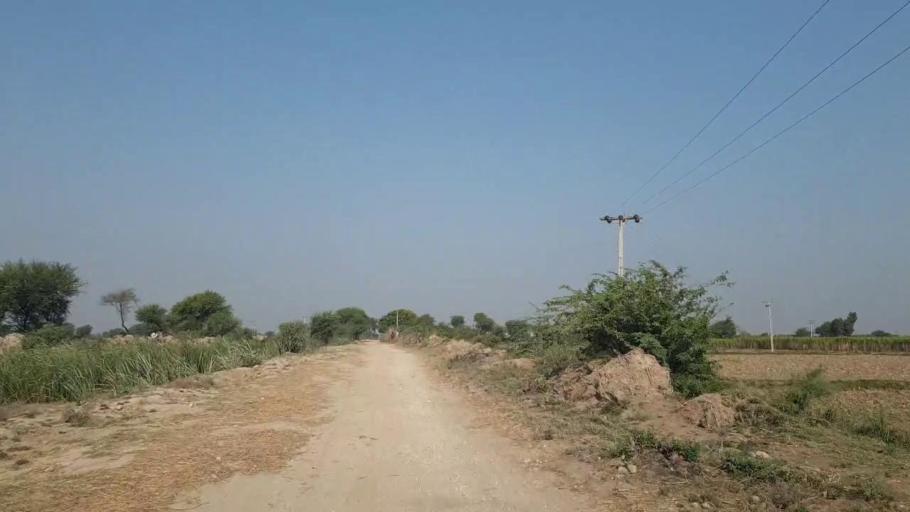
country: PK
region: Sindh
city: Matli
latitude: 24.9875
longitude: 68.6261
